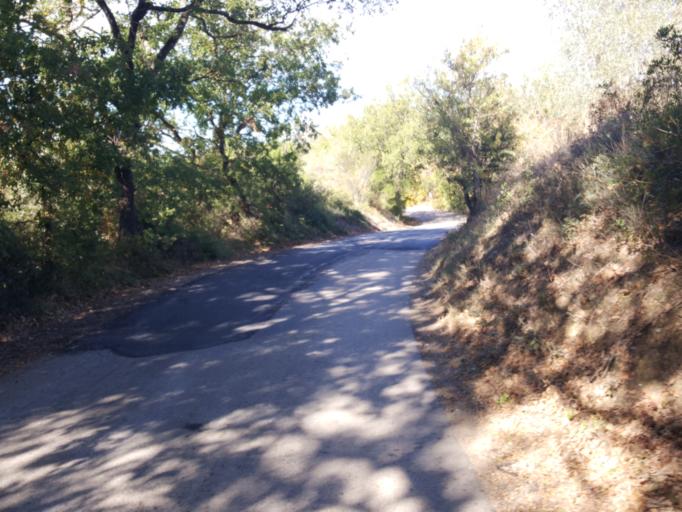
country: IT
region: Tuscany
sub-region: Provincia di Grosseto
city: Ribolla
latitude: 42.9160
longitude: 11.0132
